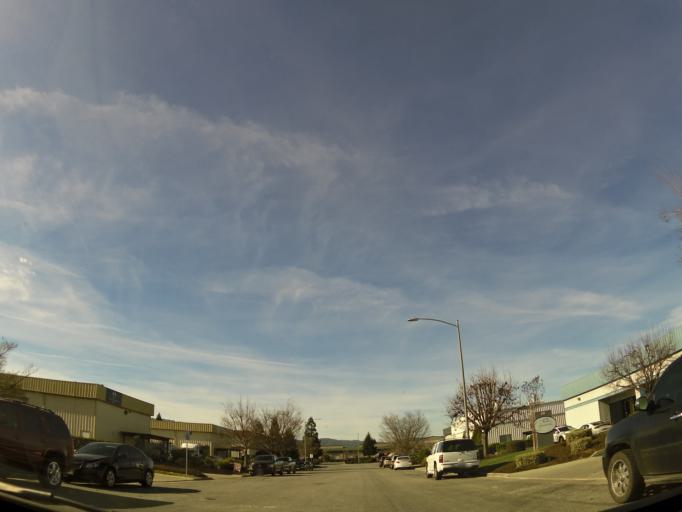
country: US
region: California
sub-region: Santa Clara County
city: Gilroy
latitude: 37.0271
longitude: -121.5734
